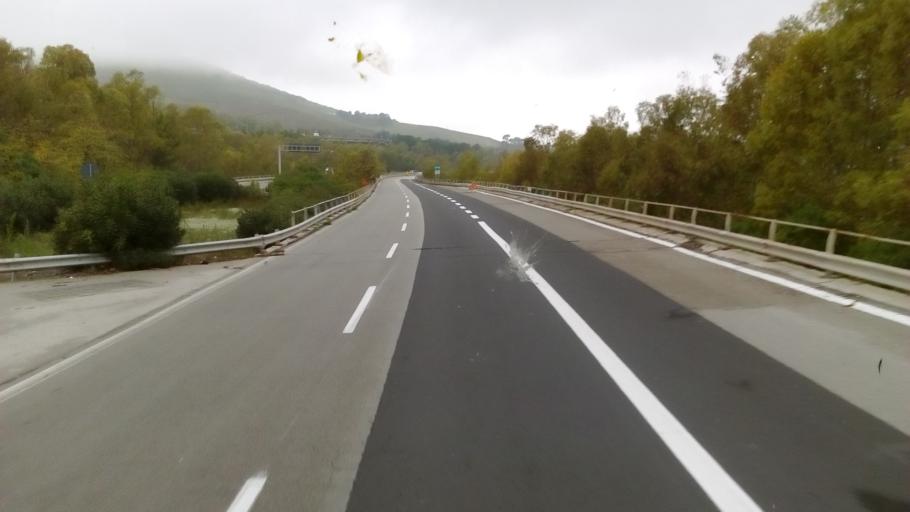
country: IT
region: Sicily
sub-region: Enna
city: Enna
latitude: 37.5789
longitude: 14.2989
